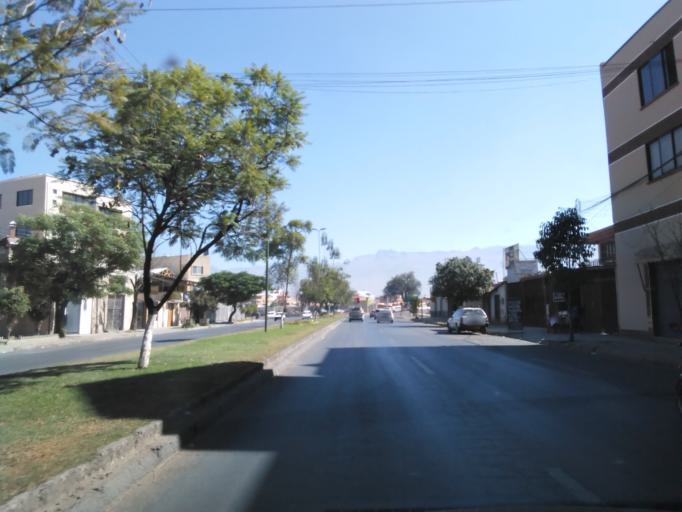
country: BO
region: Cochabamba
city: Cochabamba
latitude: -17.4022
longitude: -66.1820
